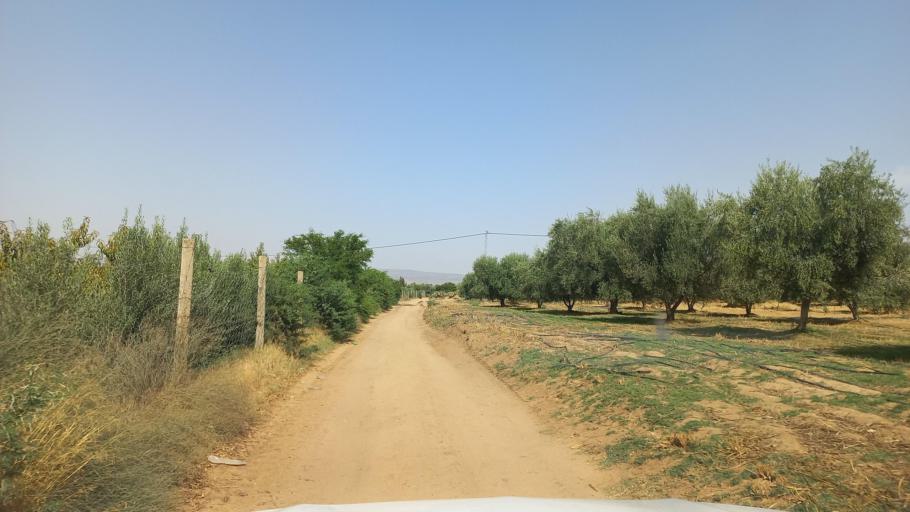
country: TN
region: Al Qasrayn
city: Kasserine
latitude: 35.2506
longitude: 9.0490
